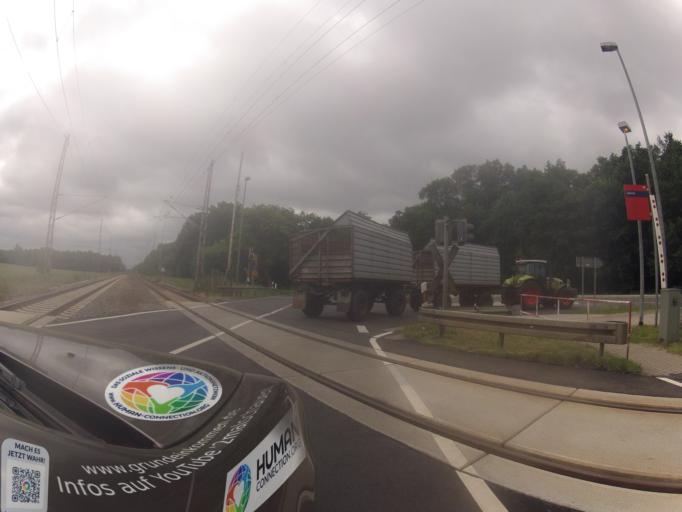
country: DE
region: Mecklenburg-Vorpommern
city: Jatznick
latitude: 53.6013
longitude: 13.9392
